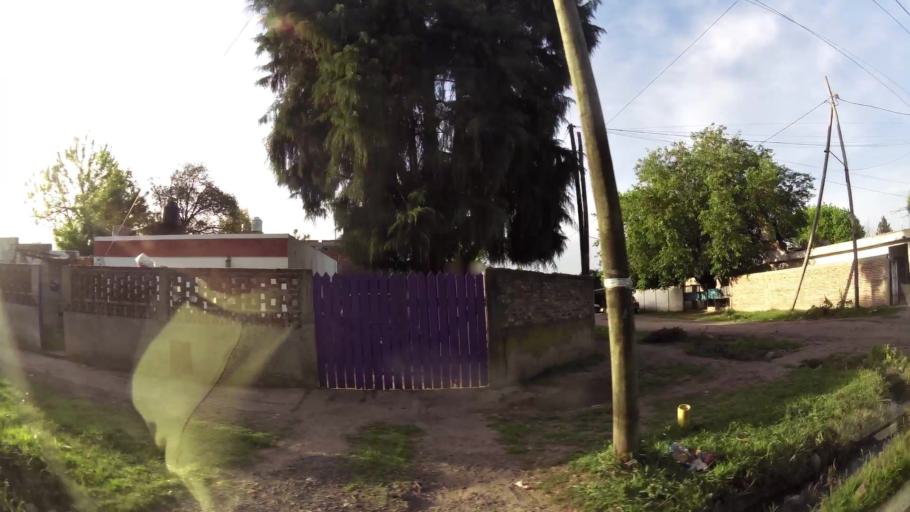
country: AR
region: Buenos Aires
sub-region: Partido de Almirante Brown
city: Adrogue
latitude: -34.7885
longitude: -58.3398
